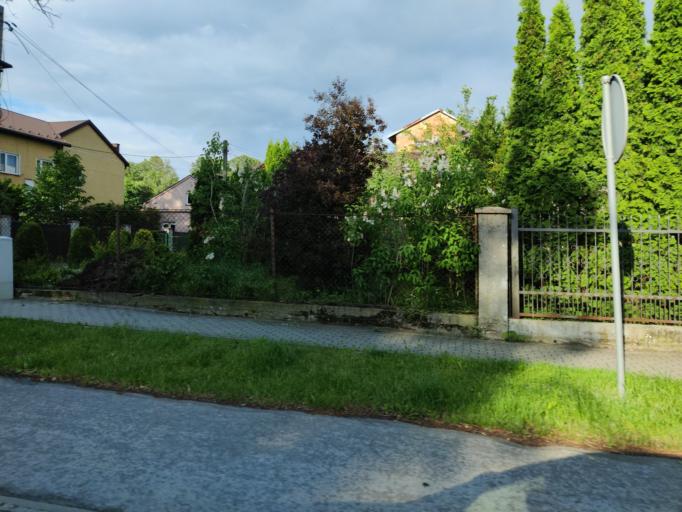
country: PL
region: Masovian Voivodeship
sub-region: Warszawa
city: Kabaty
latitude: 52.1235
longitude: 21.1029
